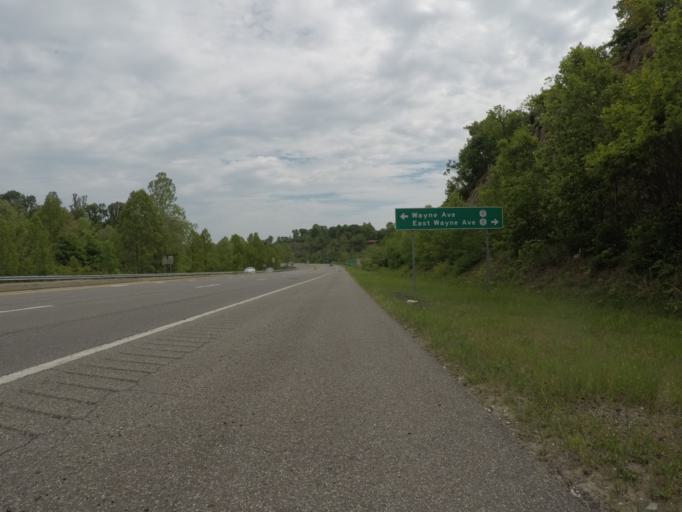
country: US
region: West Virginia
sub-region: Wayne County
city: Kenova
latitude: 38.3841
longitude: -82.5768
